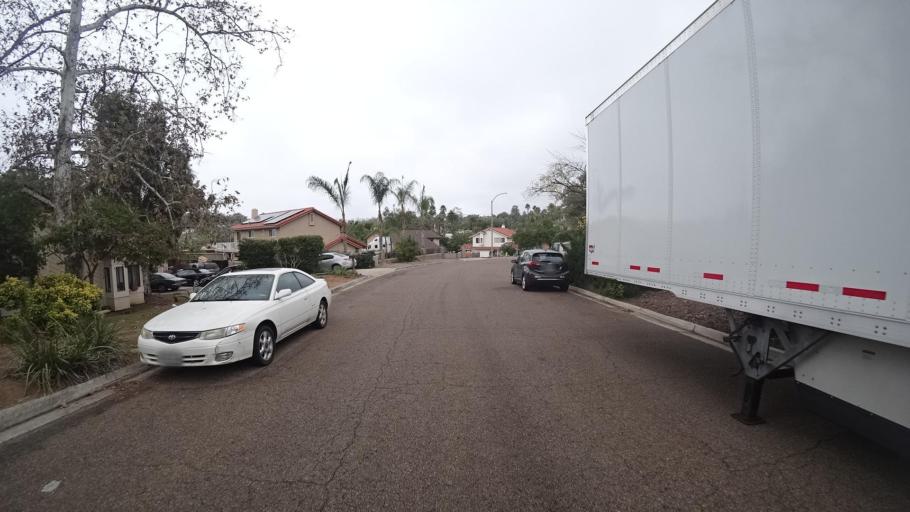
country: US
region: California
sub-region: San Diego County
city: Rancho San Diego
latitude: 32.7726
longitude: -116.9265
